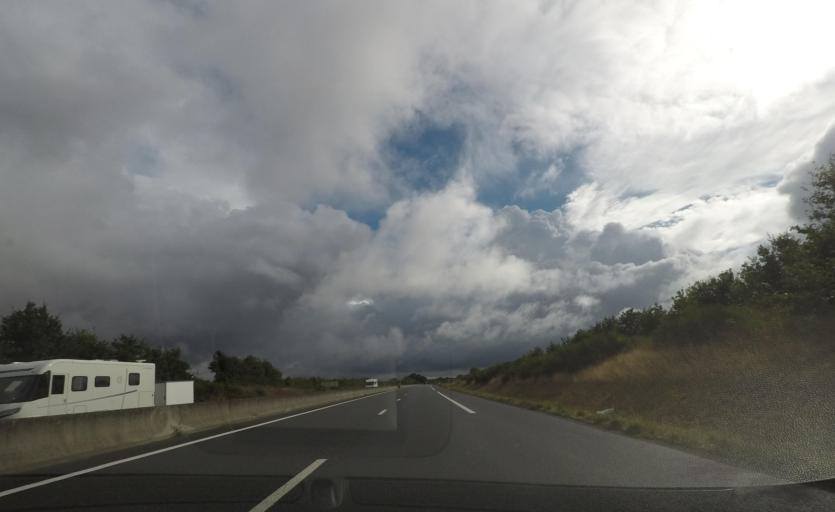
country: FR
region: Pays de la Loire
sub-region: Departement de la Vendee
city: La Roche-sur-Yon
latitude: 46.6601
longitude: -1.3747
